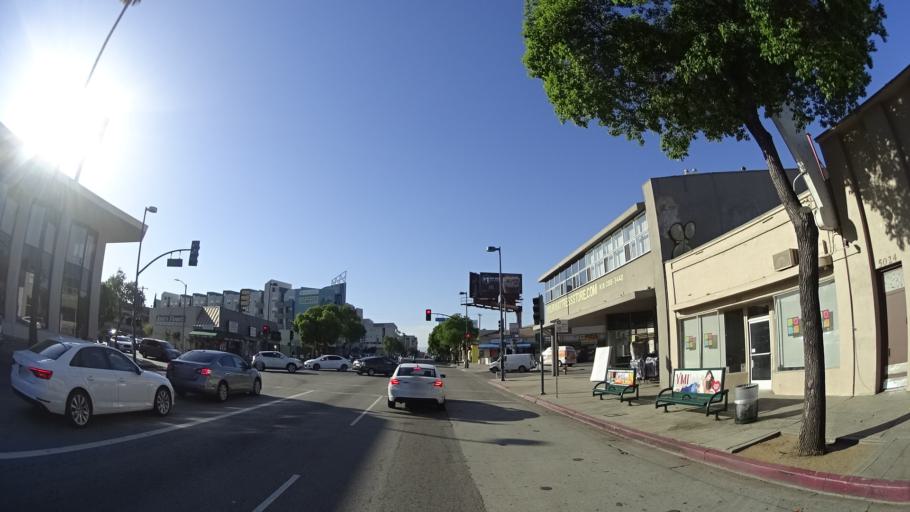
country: US
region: California
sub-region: Los Angeles County
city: North Hollywood
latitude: 34.1616
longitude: -118.3726
